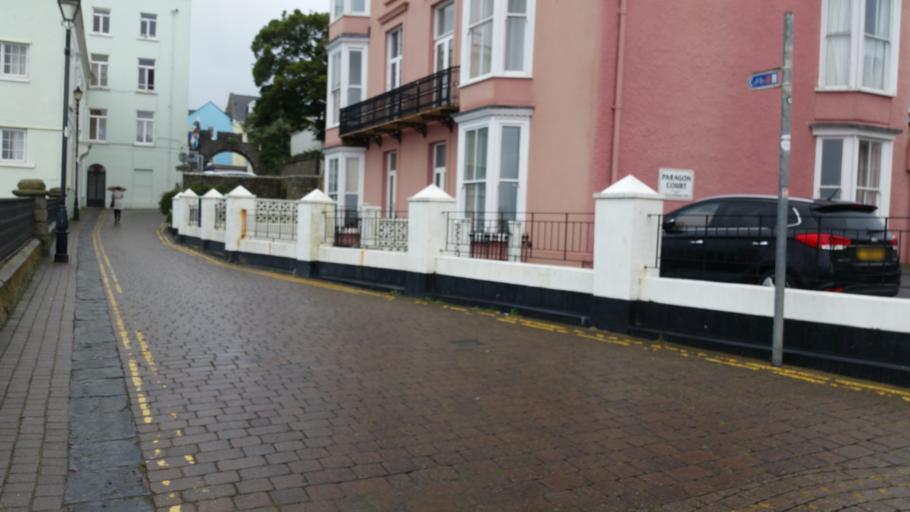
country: GB
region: Wales
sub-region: Pembrokeshire
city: Tenby
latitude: 51.6702
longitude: -4.6984
